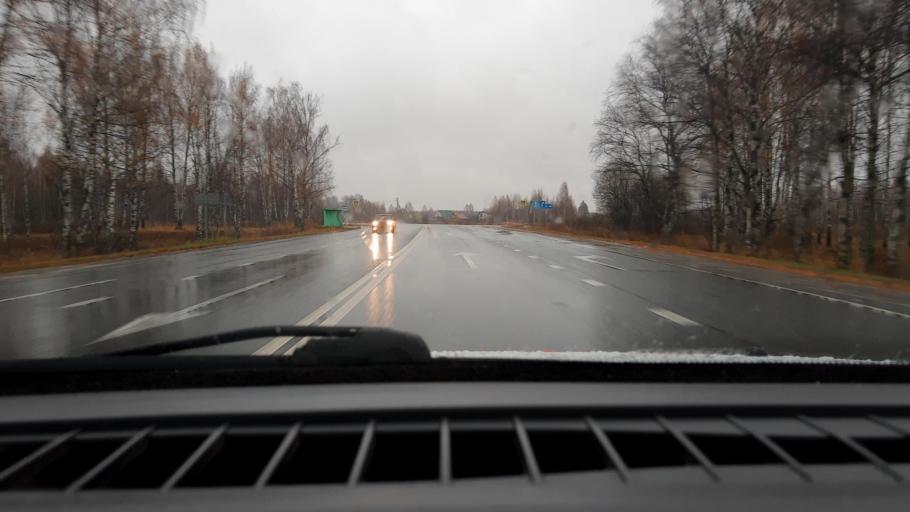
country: RU
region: Nizjnij Novgorod
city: Sitniki
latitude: 56.5235
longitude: 44.0262
